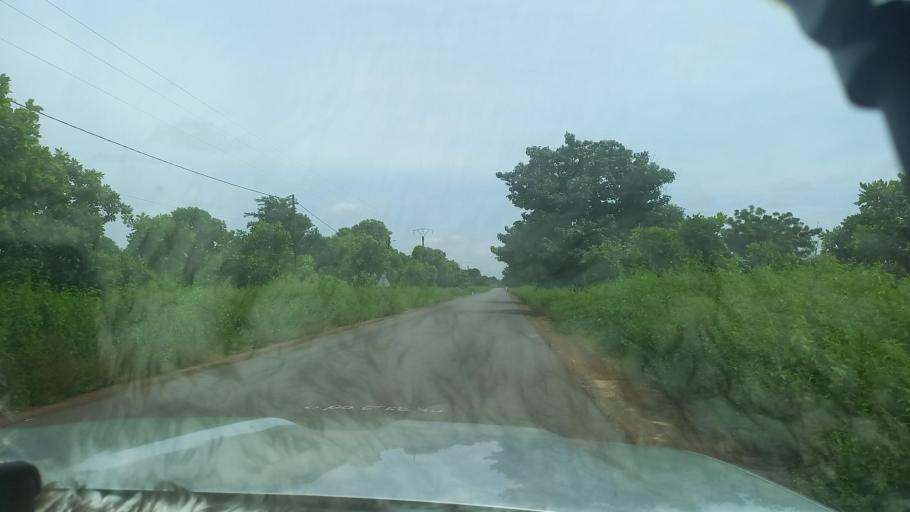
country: SN
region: Kolda
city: Marsassoum
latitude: 12.9626
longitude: -15.9821
